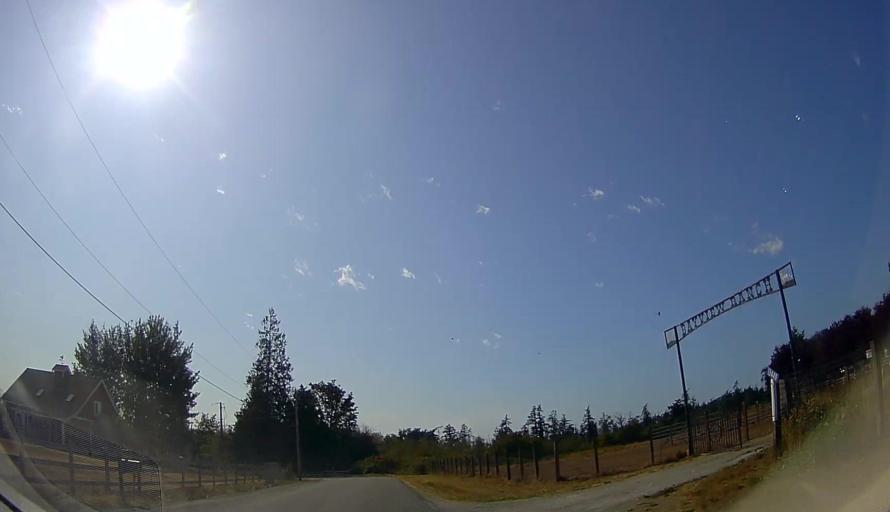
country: US
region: Washington
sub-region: Skagit County
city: Burlington
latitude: 48.4939
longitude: -122.4630
